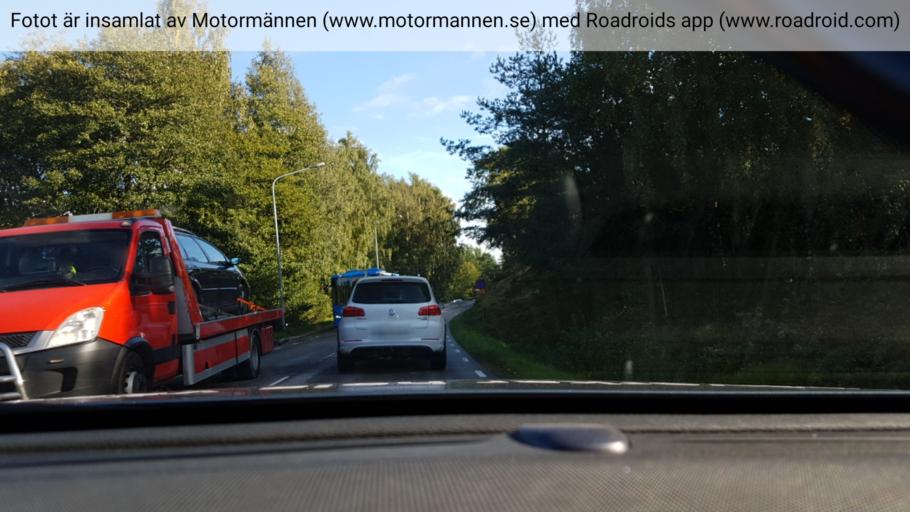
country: SE
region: Vaestra Goetaland
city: Svanesund
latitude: 58.1417
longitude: 11.8276
